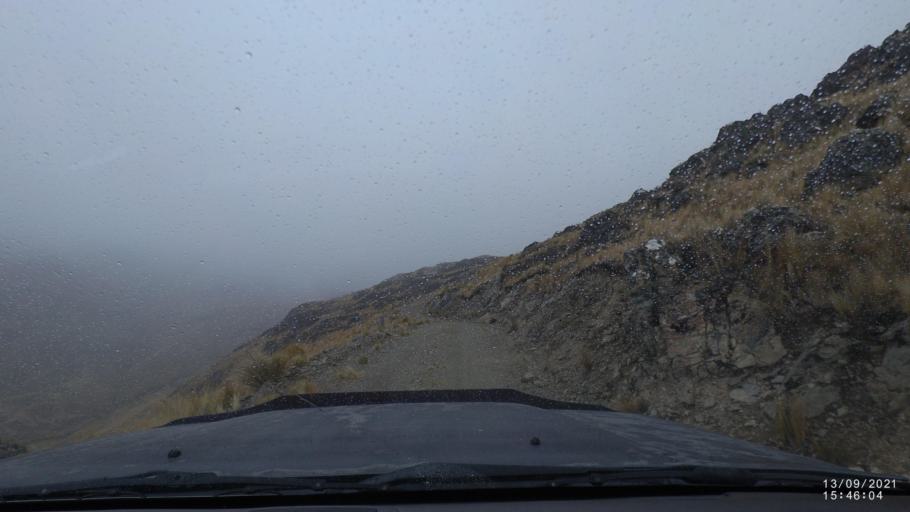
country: BO
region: Cochabamba
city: Colomi
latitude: -17.3156
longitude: -65.7215
